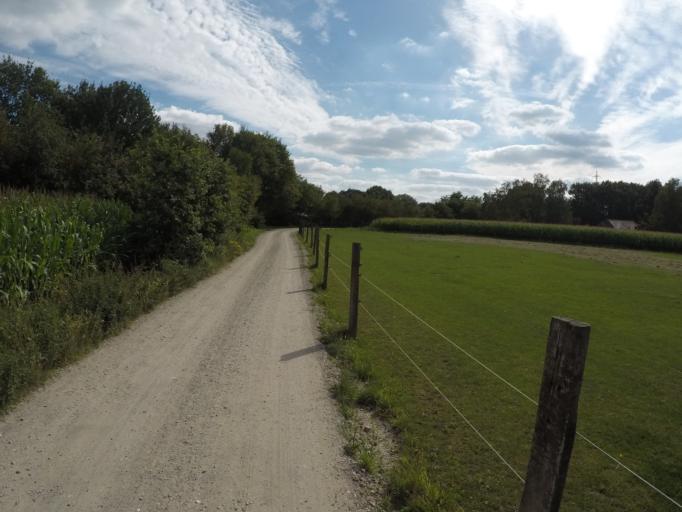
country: BE
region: Flanders
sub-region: Provincie Antwerpen
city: Nijlen
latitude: 51.1491
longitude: 4.6559
